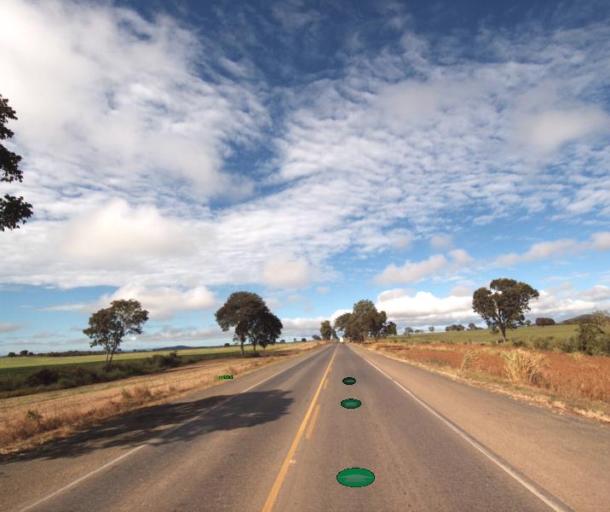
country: BR
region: Goias
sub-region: Uruacu
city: Uruacu
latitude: -14.6791
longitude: -49.2049
